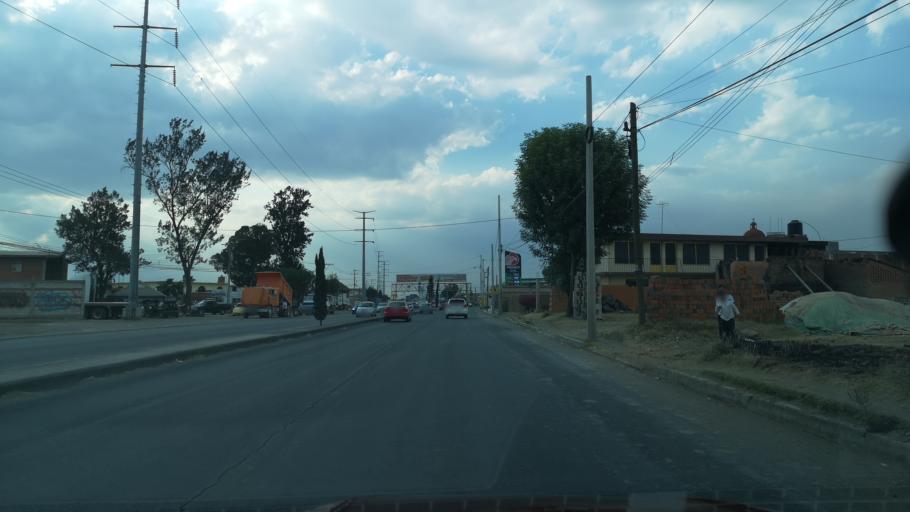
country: MX
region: Puebla
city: Cholula
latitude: 19.0802
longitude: -98.3271
